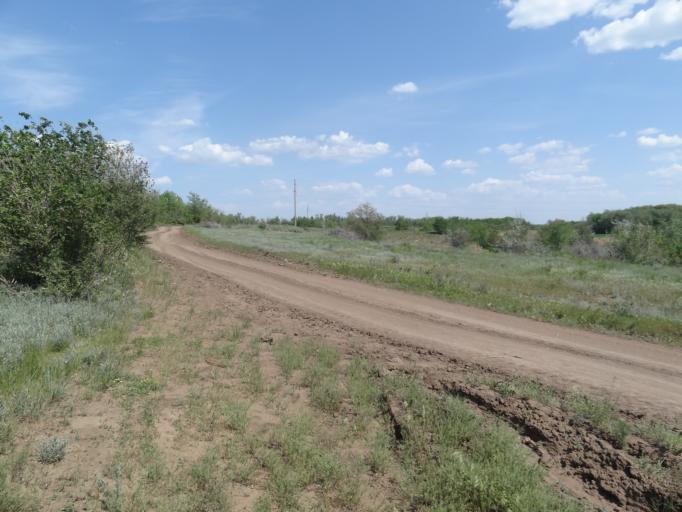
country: RU
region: Saratov
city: Privolzhskiy
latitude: 51.3470
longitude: 46.1561
